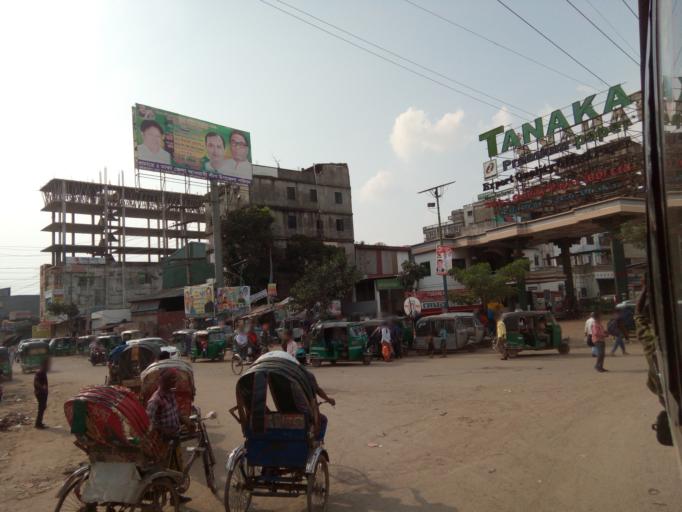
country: BD
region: Dhaka
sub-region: Dhaka
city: Dhaka
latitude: 23.7010
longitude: 90.3974
